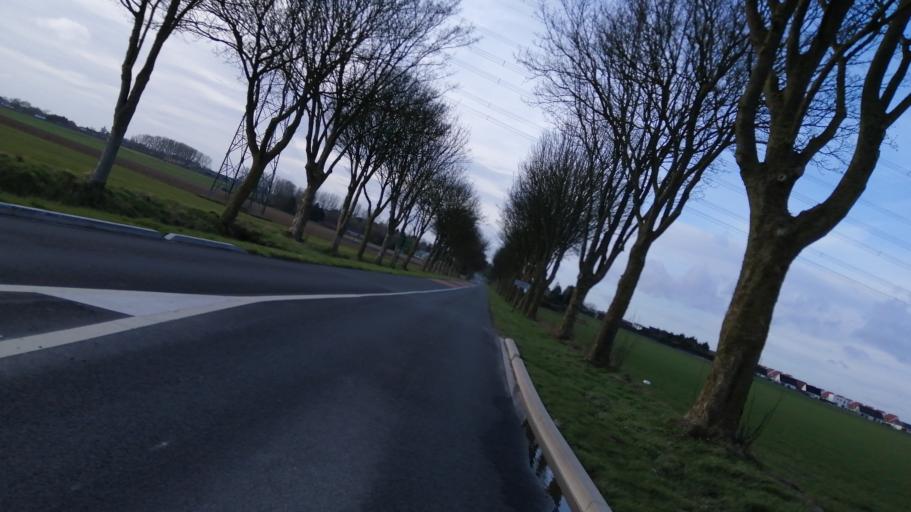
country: FR
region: Nord-Pas-de-Calais
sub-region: Departement du Pas-de-Calais
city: Beaurains
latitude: 50.2522
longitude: 2.8086
